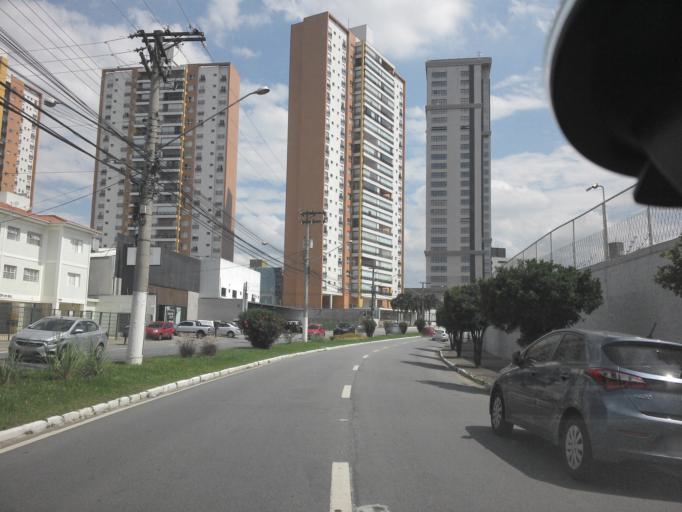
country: BR
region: Sao Paulo
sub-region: Taubate
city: Taubate
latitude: -23.0275
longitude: -45.5790
